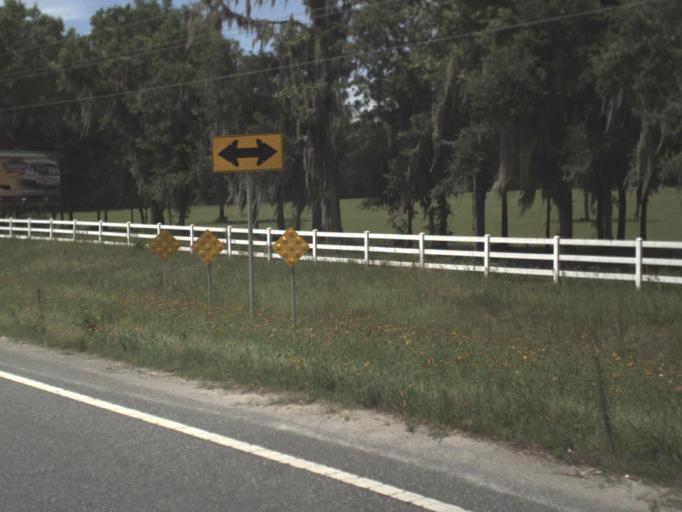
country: US
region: Florida
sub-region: Suwannee County
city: Live Oak
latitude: 30.3886
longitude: -82.9389
